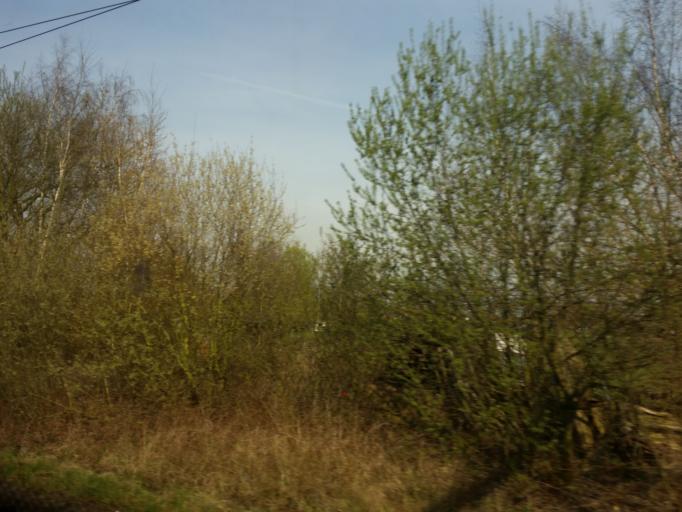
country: BE
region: Flanders
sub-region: Provincie Vlaams-Brabant
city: Zemst
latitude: 51.0136
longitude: 4.4343
